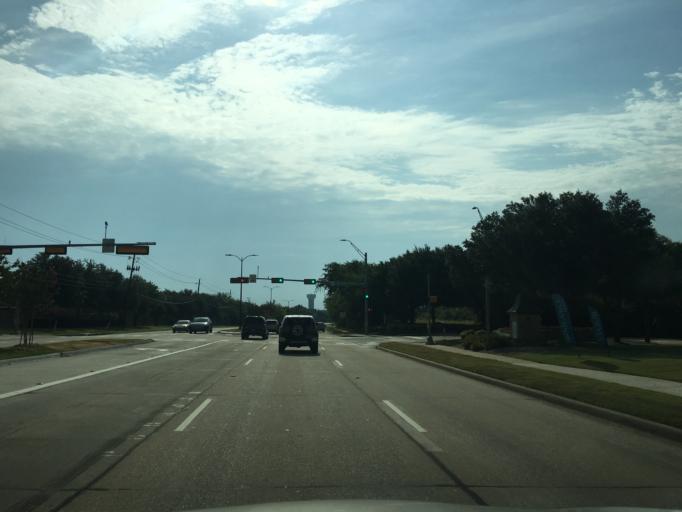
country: US
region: Texas
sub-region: Collin County
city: Fairview
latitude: 33.1986
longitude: -96.6883
